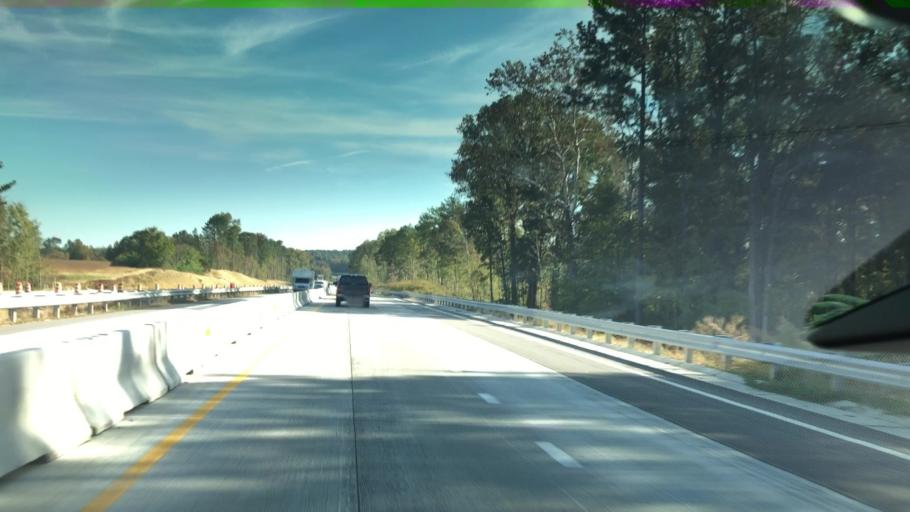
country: US
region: North Carolina
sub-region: Vance County
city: Henderson
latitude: 36.3634
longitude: -78.3717
